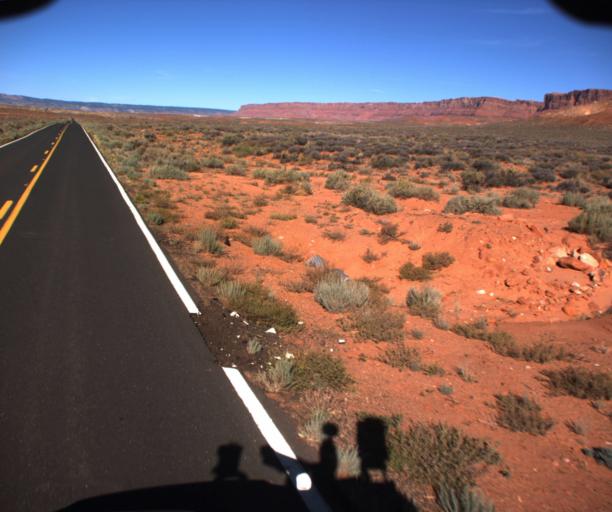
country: US
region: Arizona
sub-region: Coconino County
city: Page
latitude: 36.6849
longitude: -111.8589
